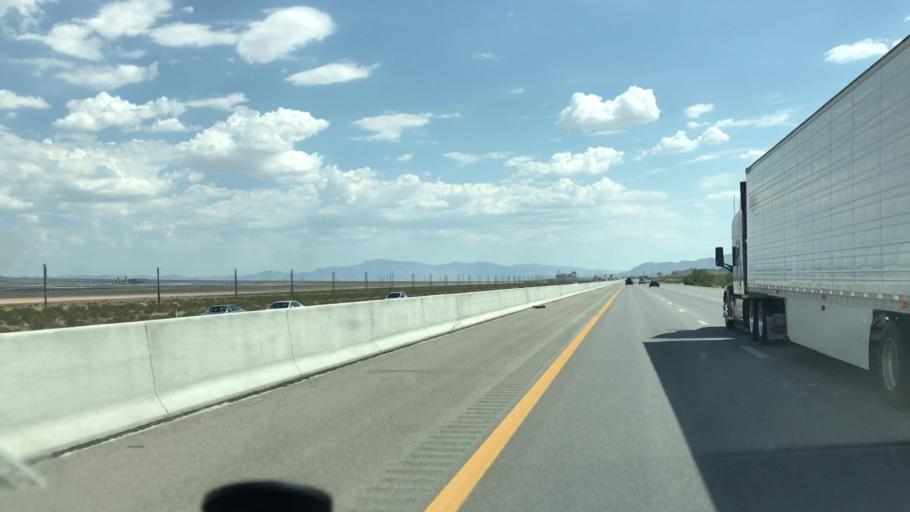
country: US
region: Nevada
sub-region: Clark County
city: Sandy Valley
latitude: 35.6579
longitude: -115.3808
